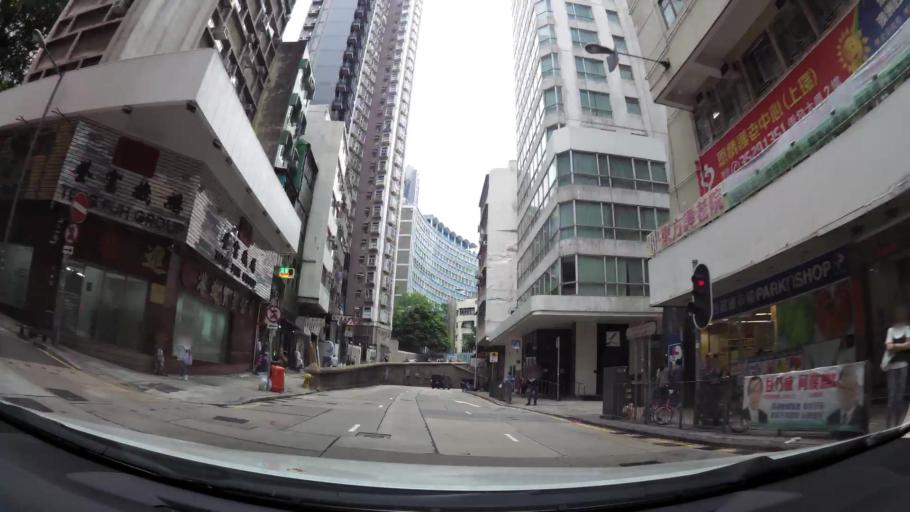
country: HK
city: Hong Kong
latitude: 22.2864
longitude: 114.1485
